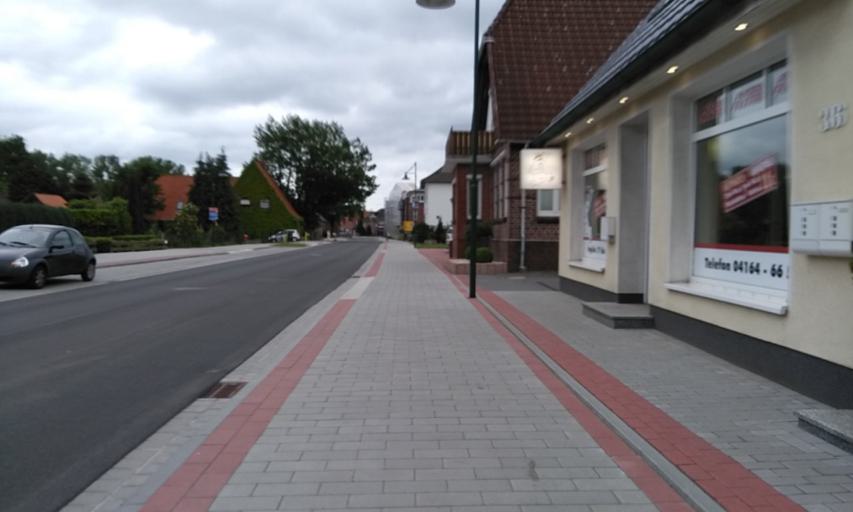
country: DE
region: Lower Saxony
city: Harsefeld
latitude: 53.4574
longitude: 9.5001
